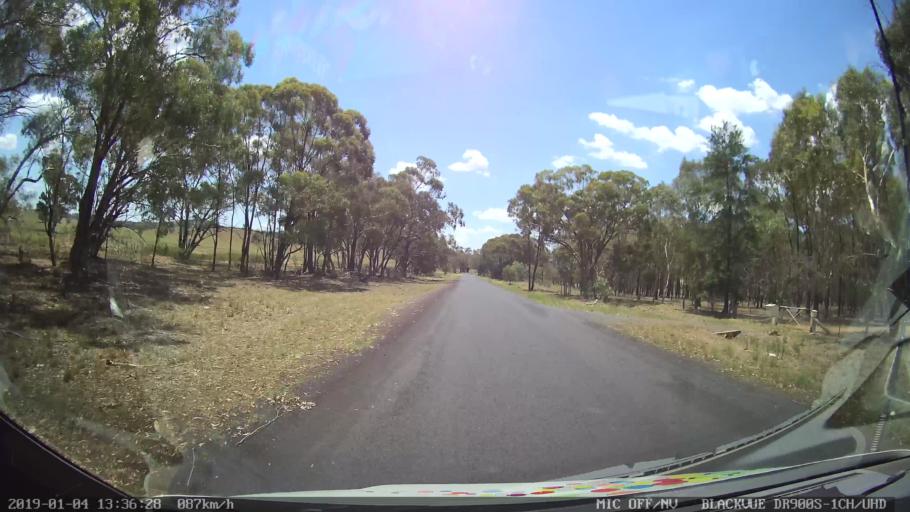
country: AU
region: New South Wales
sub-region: Dubbo Municipality
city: Dubbo
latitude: -32.5604
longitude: 148.5376
